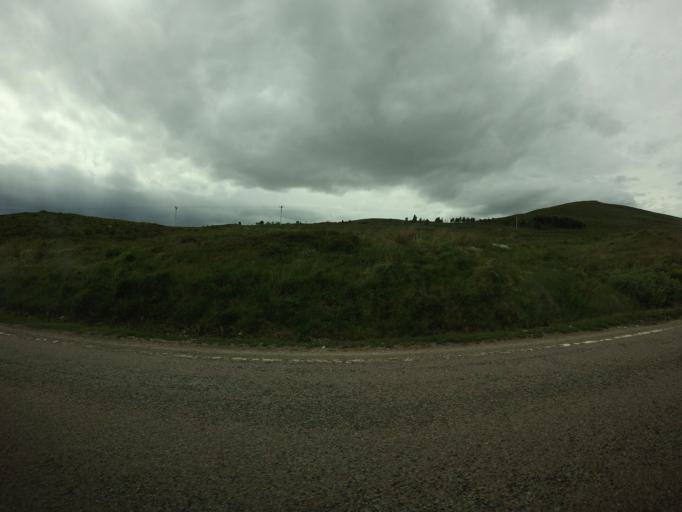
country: GB
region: Scotland
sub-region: Highland
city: Muir of Ord
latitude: 57.6964
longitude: -4.7970
